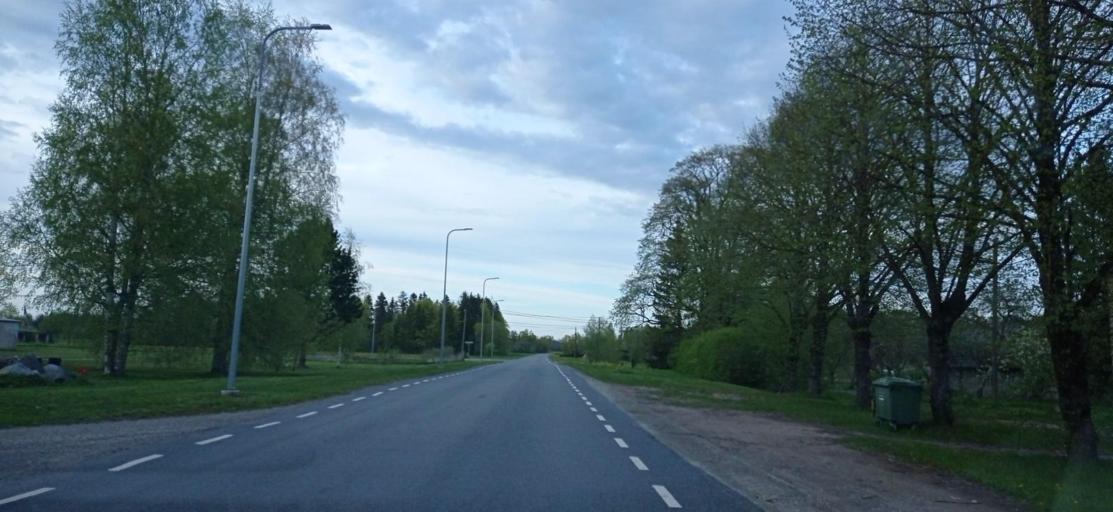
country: EE
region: Paernumaa
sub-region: Tootsi vald
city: Tootsi
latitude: 58.5275
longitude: 24.7037
